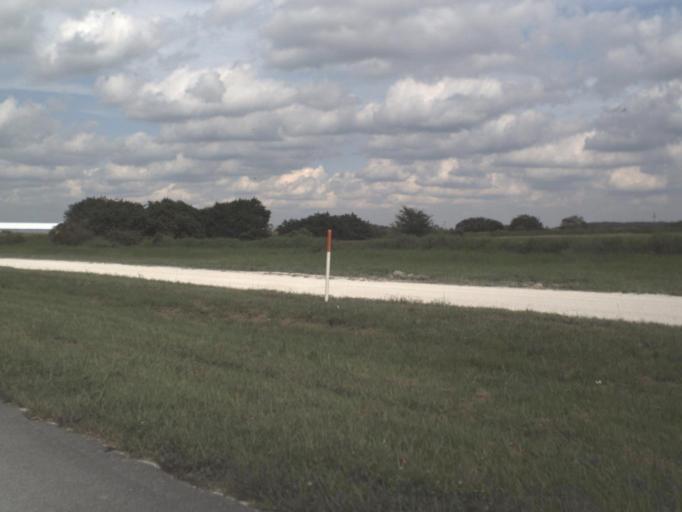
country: US
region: Florida
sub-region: Okeechobee County
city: Cypress Quarters
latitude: 27.4157
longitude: -80.8136
